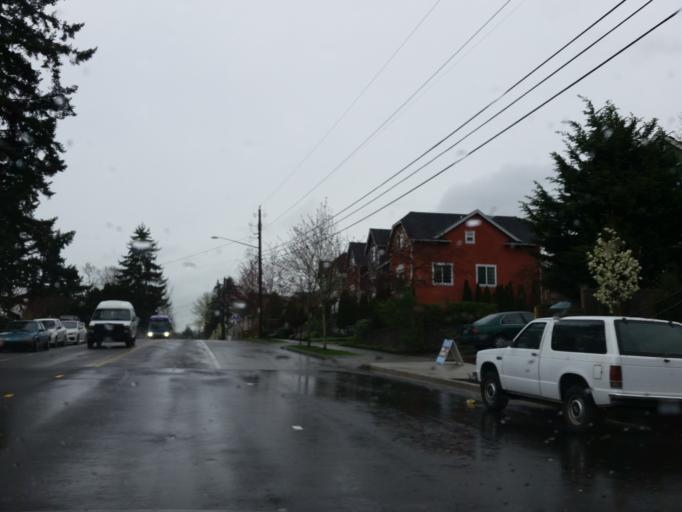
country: US
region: Washington
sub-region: Snohomish County
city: Martha Lake
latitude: 47.8583
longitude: -122.2542
